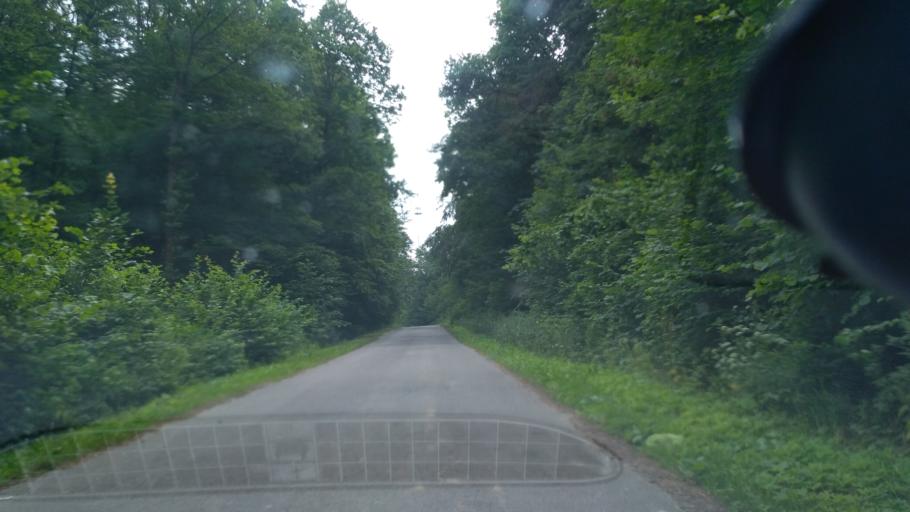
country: PL
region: Subcarpathian Voivodeship
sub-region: Powiat przeworski
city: Lopuszka Wielka
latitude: 49.9079
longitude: 22.3993
